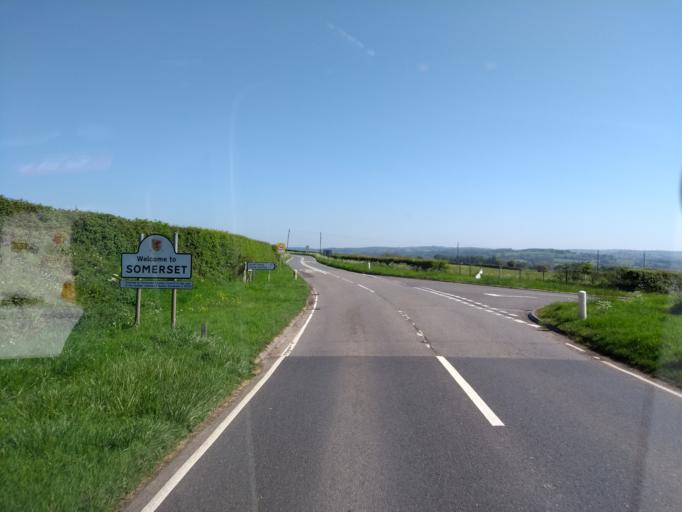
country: GB
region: England
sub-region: Somerset
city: Chard
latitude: 50.8305
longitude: -2.9638
